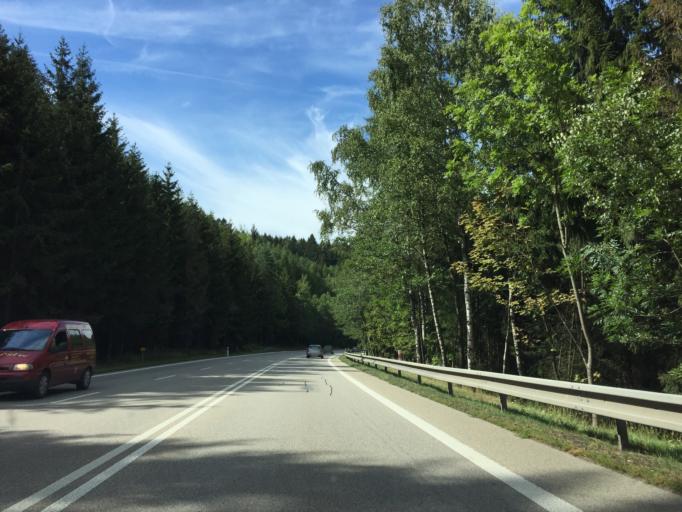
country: CZ
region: Central Bohemia
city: Votice
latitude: 49.6233
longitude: 14.6537
